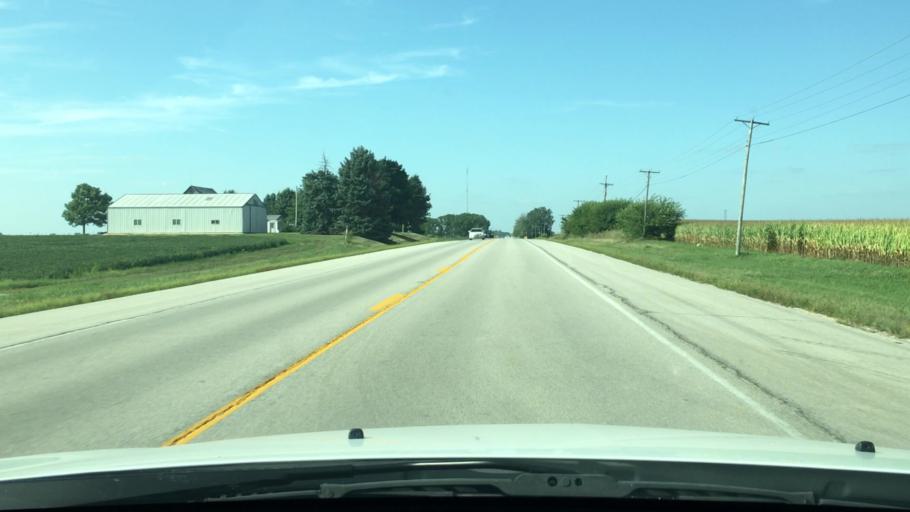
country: US
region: Illinois
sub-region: DeKalb County
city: DeKalb
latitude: 41.8582
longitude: -88.7538
